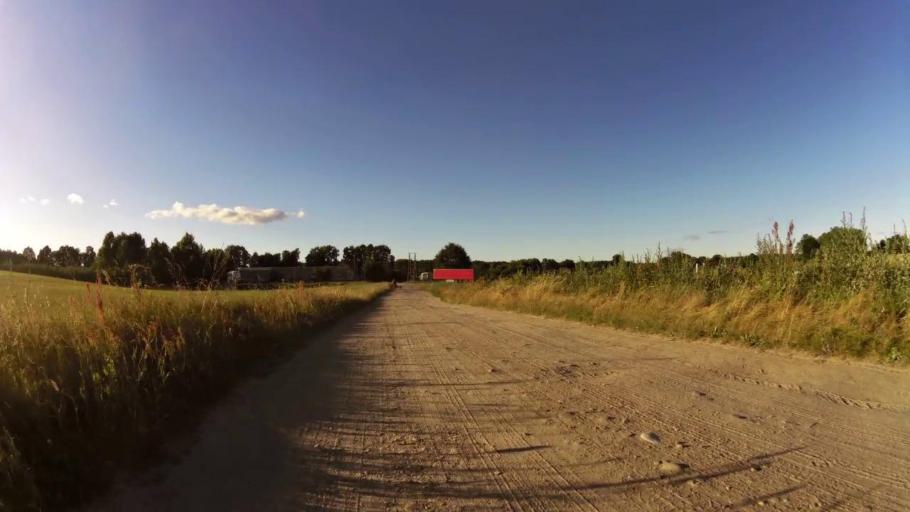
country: PL
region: West Pomeranian Voivodeship
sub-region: Powiat swidwinski
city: Swidwin
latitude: 53.7419
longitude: 15.8604
